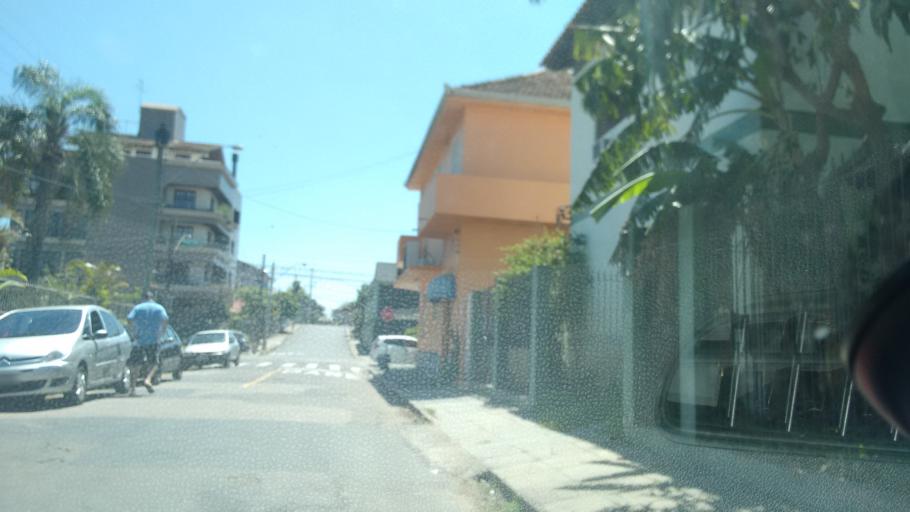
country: BR
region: Rio Grande do Sul
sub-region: Cachoeirinha
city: Cachoeirinha
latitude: -29.9968
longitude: -51.1283
